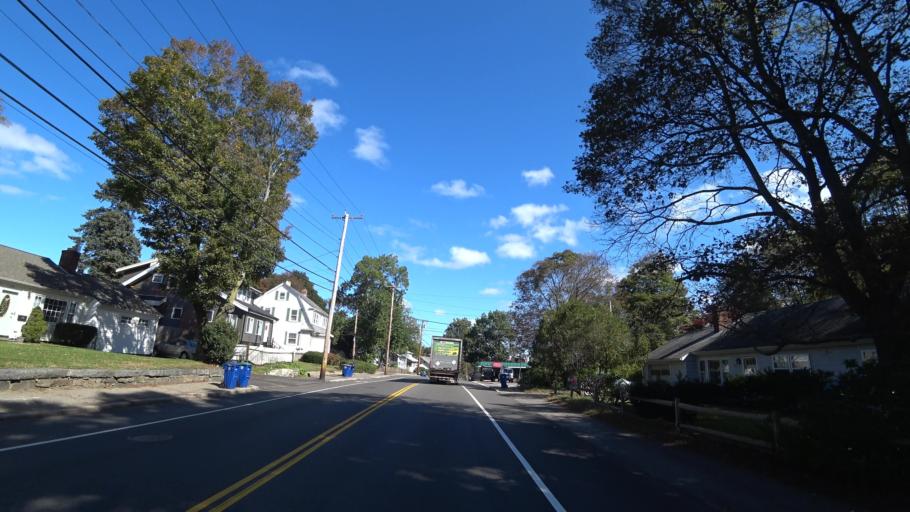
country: US
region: Massachusetts
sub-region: Norfolk County
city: Braintree
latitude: 42.2261
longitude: -70.9934
